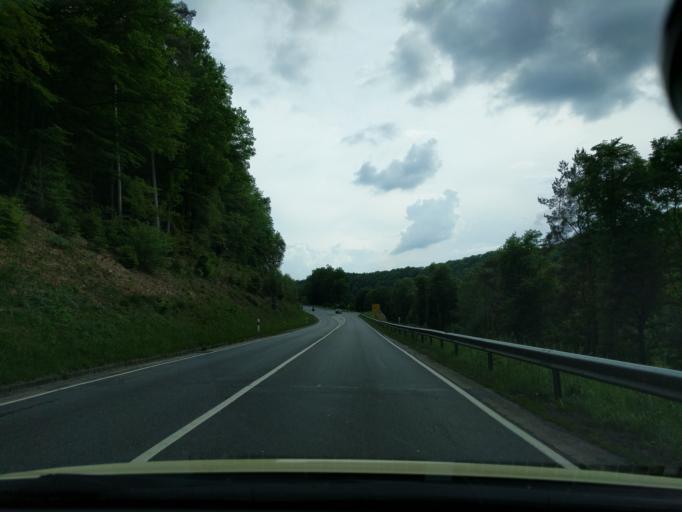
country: DE
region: Rheinland-Pfalz
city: Schopp
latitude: 49.3619
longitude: 7.6907
